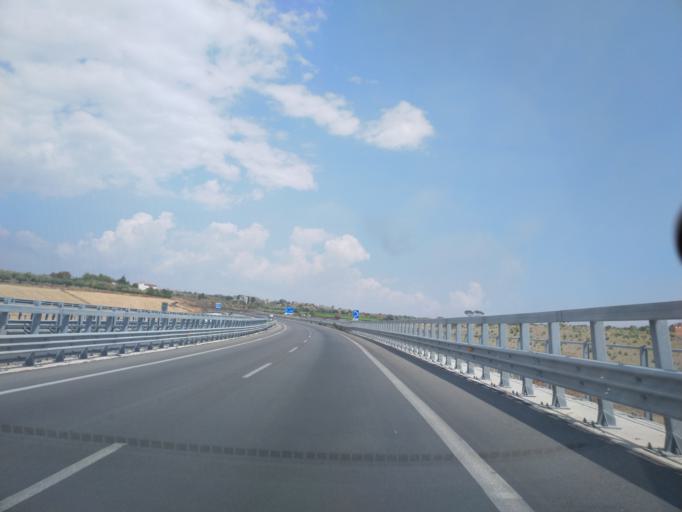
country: IT
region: Sicily
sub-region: Agrigento
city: Favara
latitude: 37.3488
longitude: 13.6720
